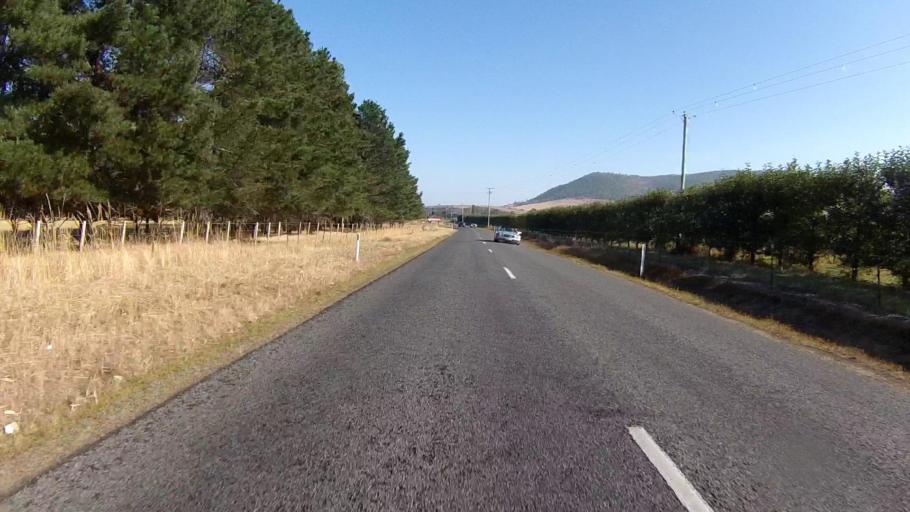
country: AU
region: Tasmania
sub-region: Derwent Valley
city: New Norfolk
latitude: -42.7510
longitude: 146.9753
